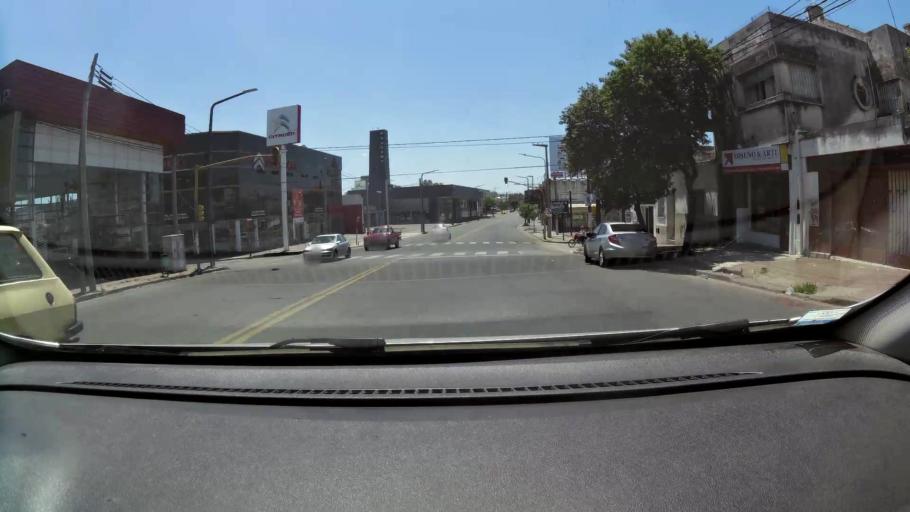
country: AR
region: Cordoba
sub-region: Departamento de Capital
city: Cordoba
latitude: -31.3959
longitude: -64.2010
